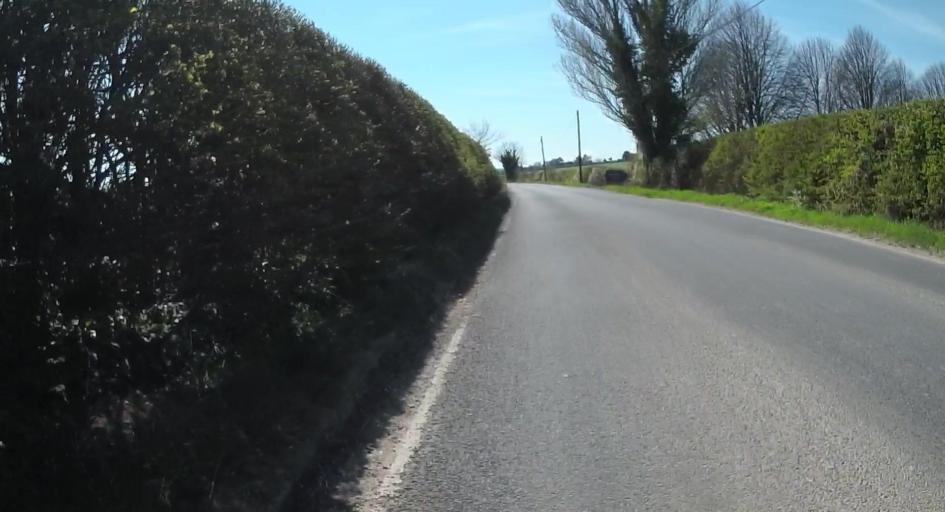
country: GB
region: England
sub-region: Hampshire
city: Romsey
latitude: 51.0863
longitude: -1.4684
